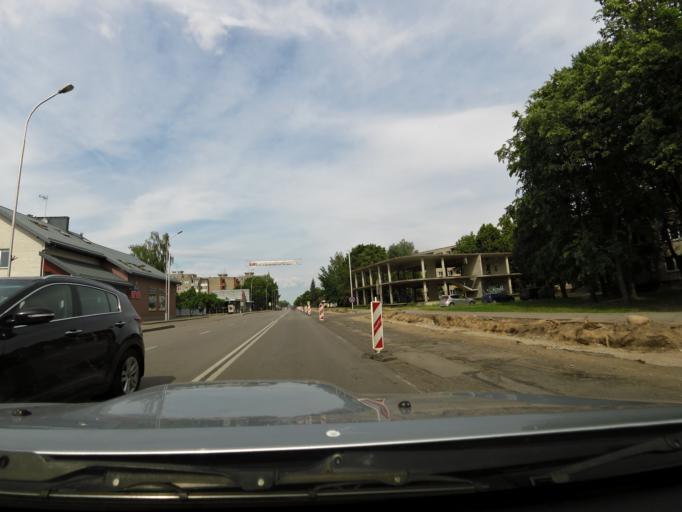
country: LT
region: Marijampoles apskritis
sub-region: Marijampole Municipality
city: Marijampole
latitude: 54.5655
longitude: 23.3573
